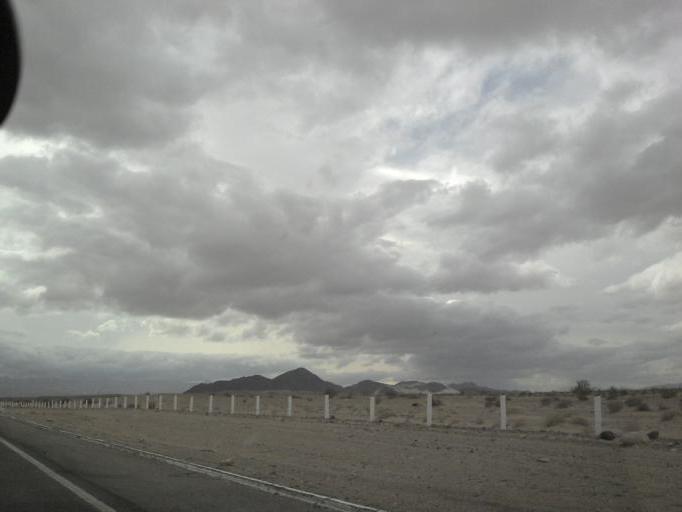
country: MX
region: Baja California
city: Progreso
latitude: 32.5700
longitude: -115.8204
